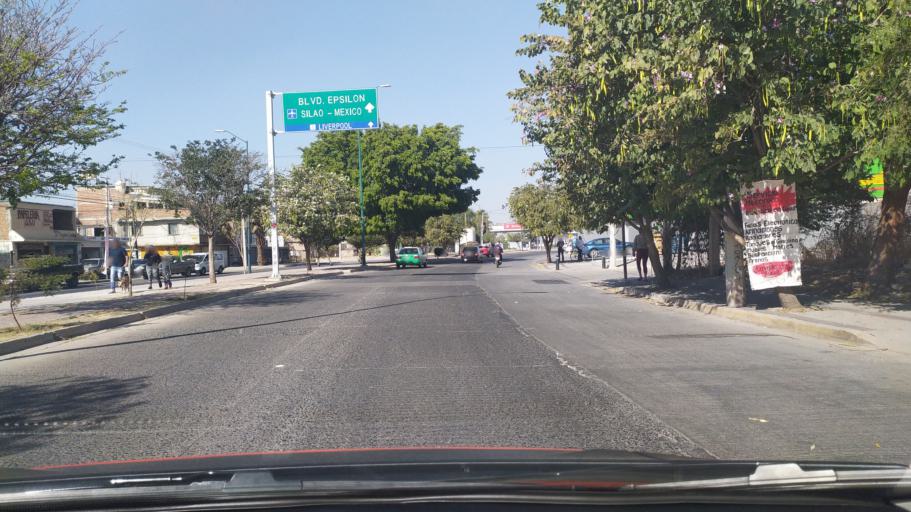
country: MX
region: Guanajuato
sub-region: Leon
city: San Jose de Duran (Los Troncoso)
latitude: 21.0745
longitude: -101.6362
